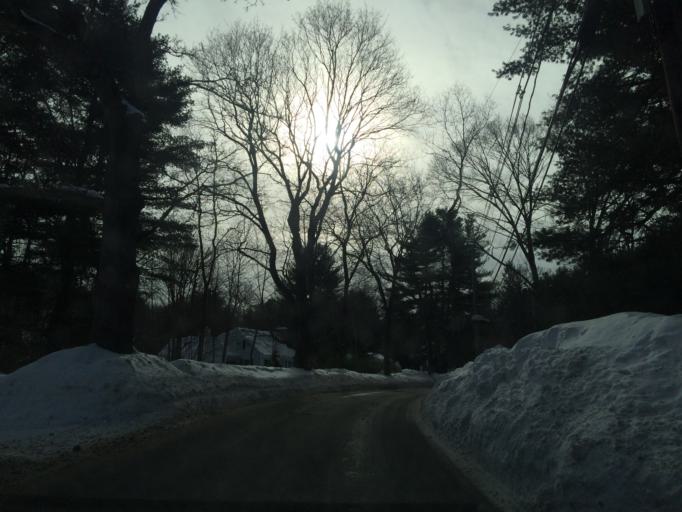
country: US
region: Massachusetts
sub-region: Middlesex County
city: Weston
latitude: 42.3646
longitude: -71.2762
